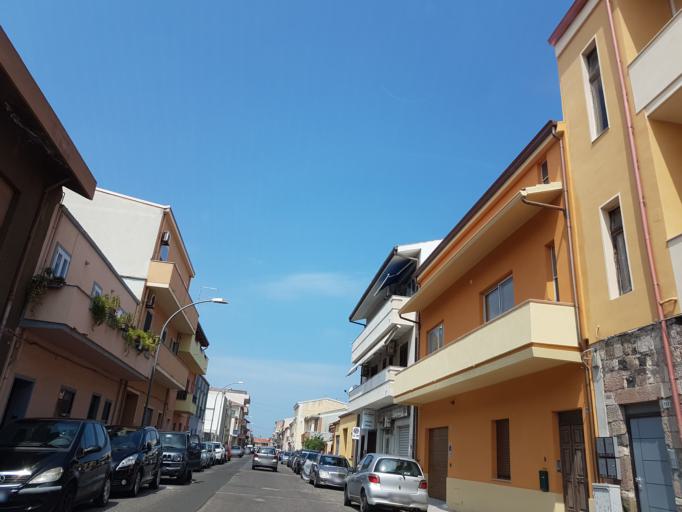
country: IT
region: Sardinia
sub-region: Provincia di Oristano
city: Oristano
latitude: 39.9095
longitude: 8.5956
